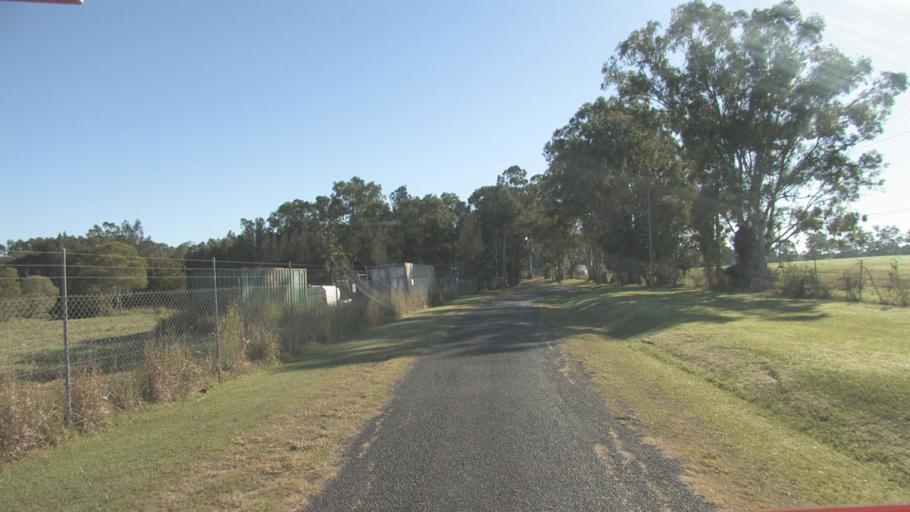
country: AU
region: Queensland
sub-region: Gold Coast
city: Yatala
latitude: -27.6921
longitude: 153.2796
